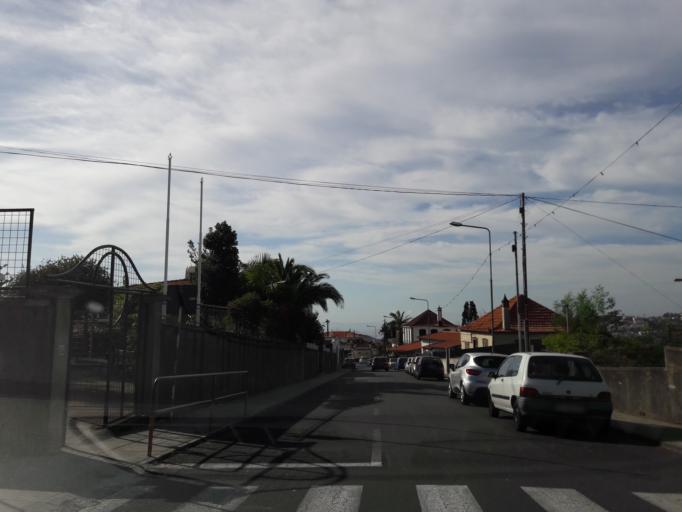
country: PT
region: Madeira
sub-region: Funchal
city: Nossa Senhora do Monte
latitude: 32.6697
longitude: -16.9227
